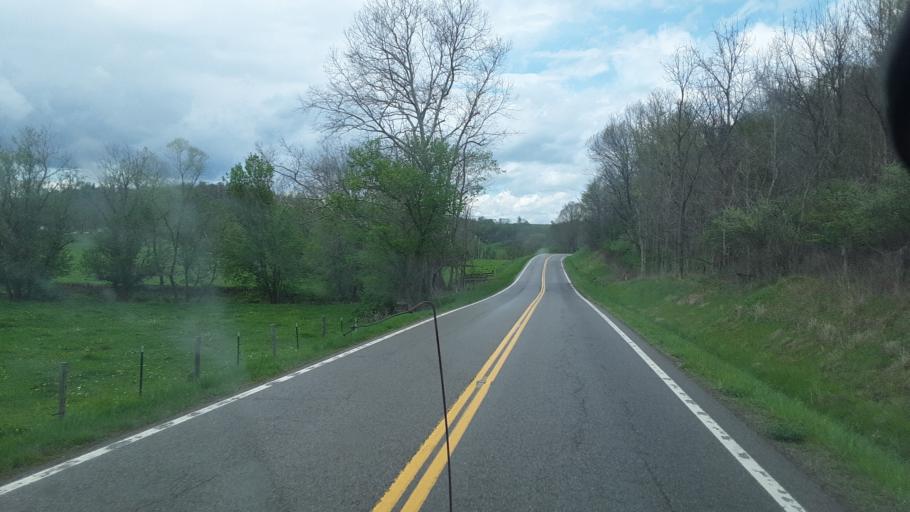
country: US
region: Ohio
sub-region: Guernsey County
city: Mantua
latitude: 40.1047
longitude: -81.7660
